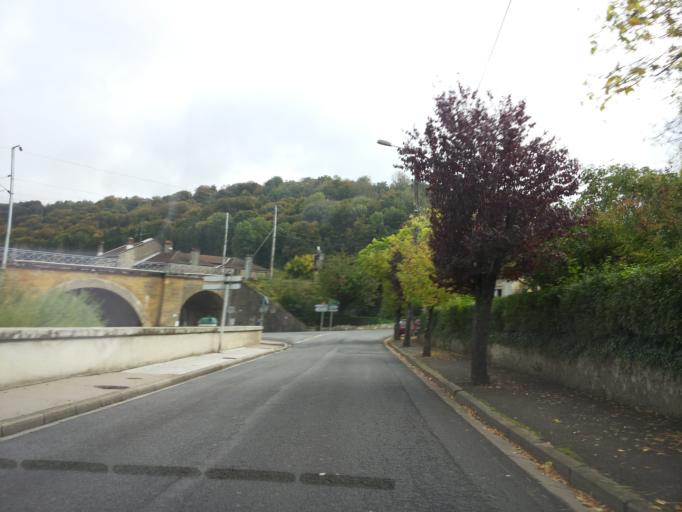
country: FR
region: Lorraine
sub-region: Departement de Meurthe-et-Moselle
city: Longuyon
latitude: 49.4473
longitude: 5.5984
